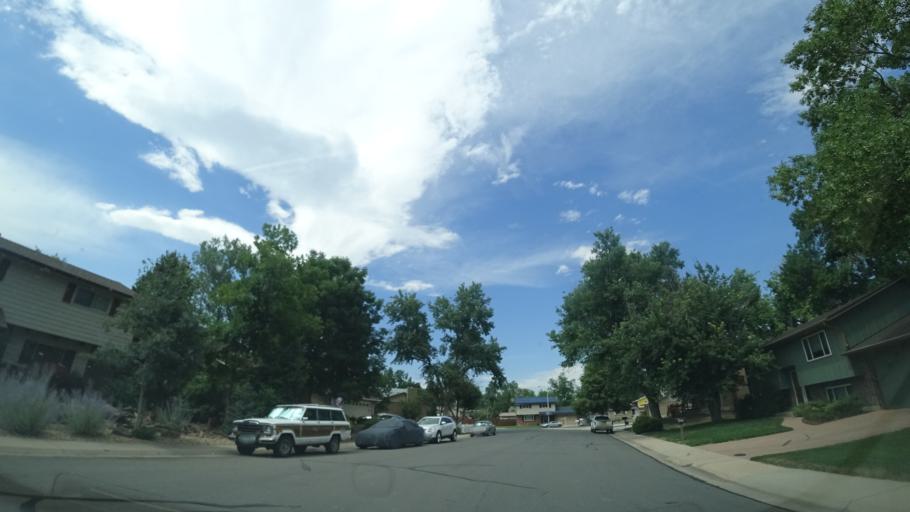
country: US
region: Colorado
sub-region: Jefferson County
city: Lakewood
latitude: 39.6945
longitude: -105.1091
